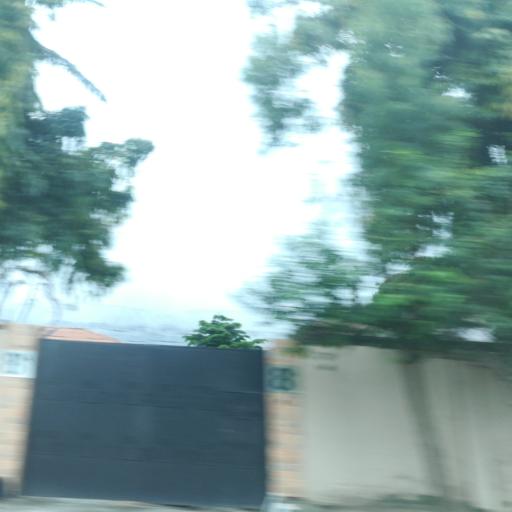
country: NG
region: Lagos
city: Ikoyi
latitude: 6.4544
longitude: 3.4470
